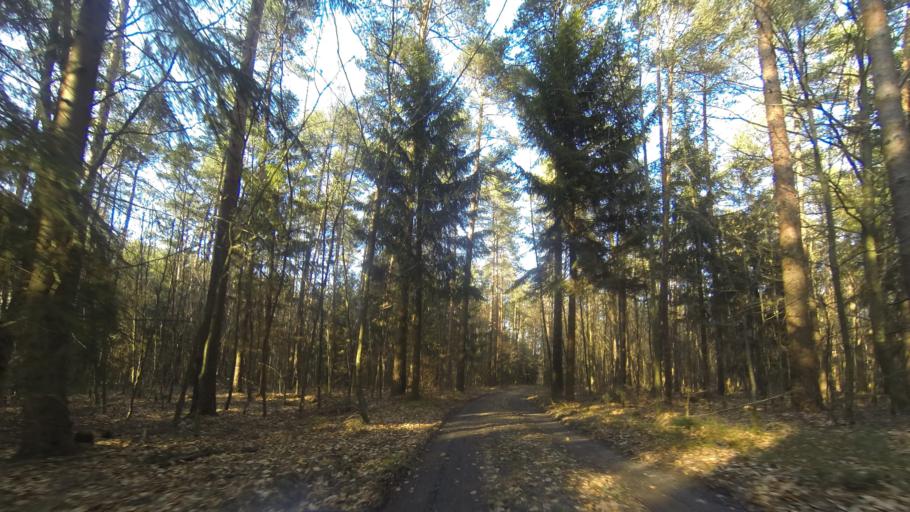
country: DE
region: Saxony
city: Laussnitz
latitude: 51.2533
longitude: 13.8425
